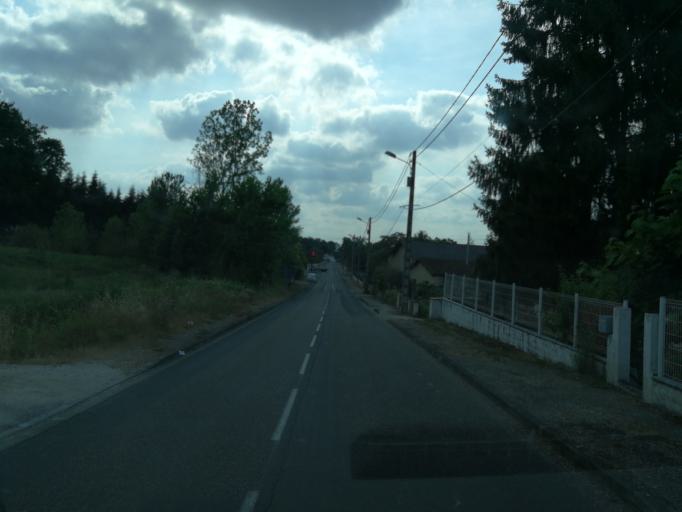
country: FR
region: Aquitaine
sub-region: Departement du Lot-et-Garonne
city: Fumel
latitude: 44.5030
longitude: 0.9597
